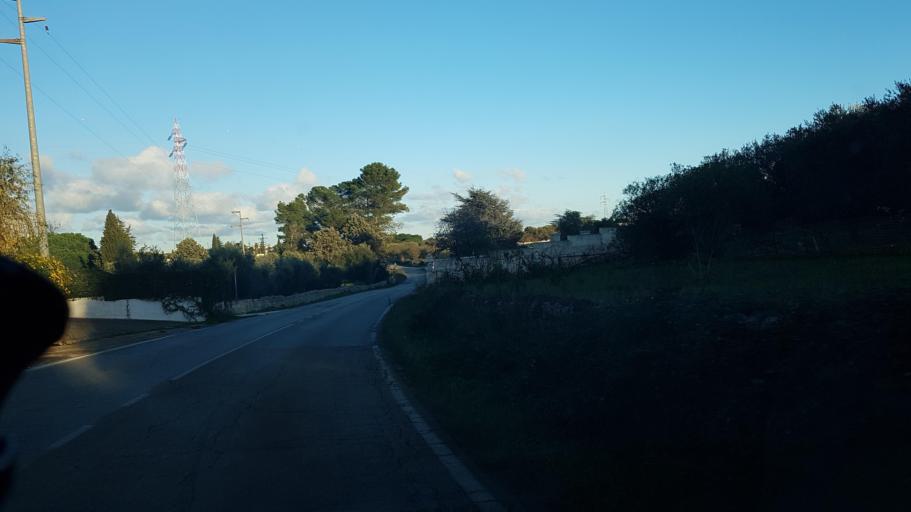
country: IT
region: Apulia
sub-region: Provincia di Brindisi
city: Ostuni
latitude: 40.7111
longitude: 17.5469
